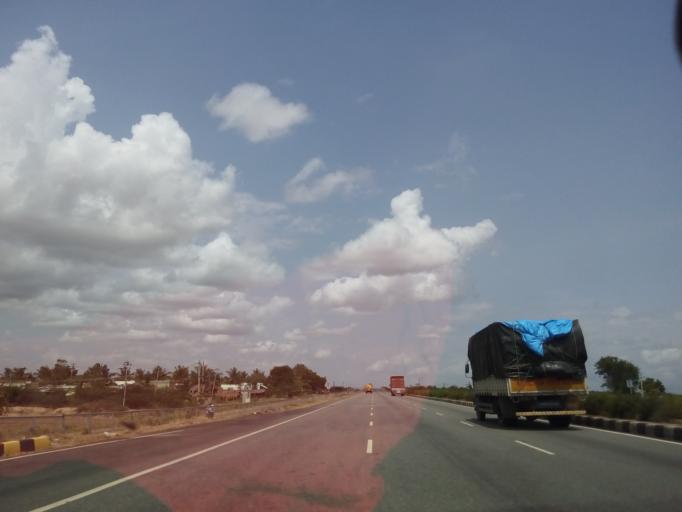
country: IN
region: Karnataka
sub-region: Tumkur
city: Sira
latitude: 13.7788
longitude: 76.8320
